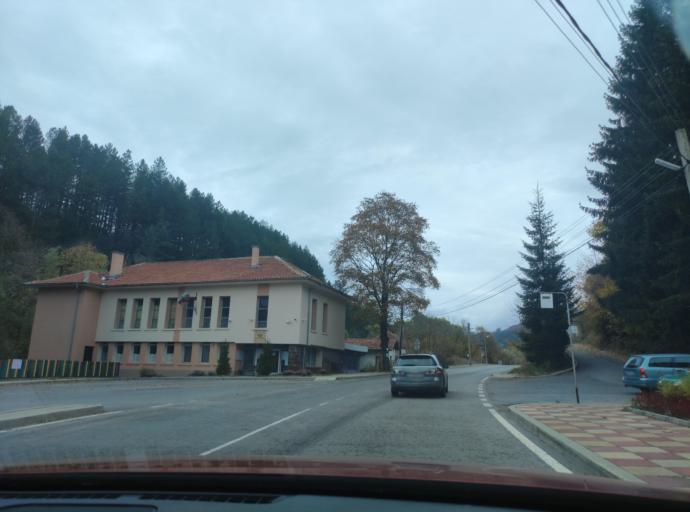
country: BG
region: Sofiya
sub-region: Obshtina Godech
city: Godech
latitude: 43.0728
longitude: 23.1084
